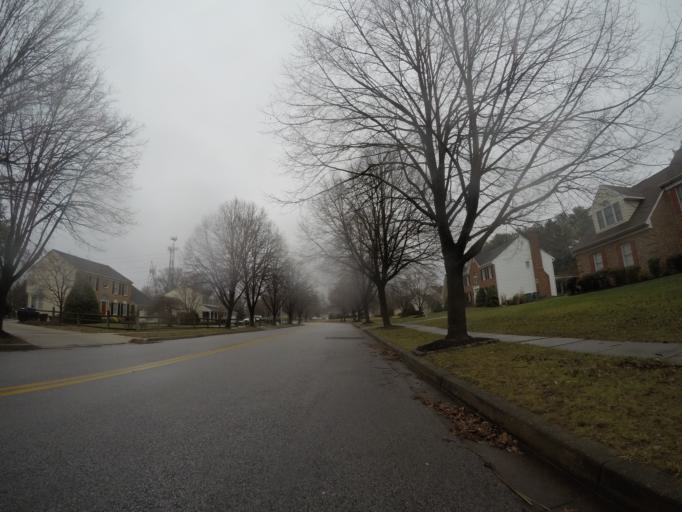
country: US
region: Maryland
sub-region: Howard County
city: Ellicott City
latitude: 39.2464
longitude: -76.8054
